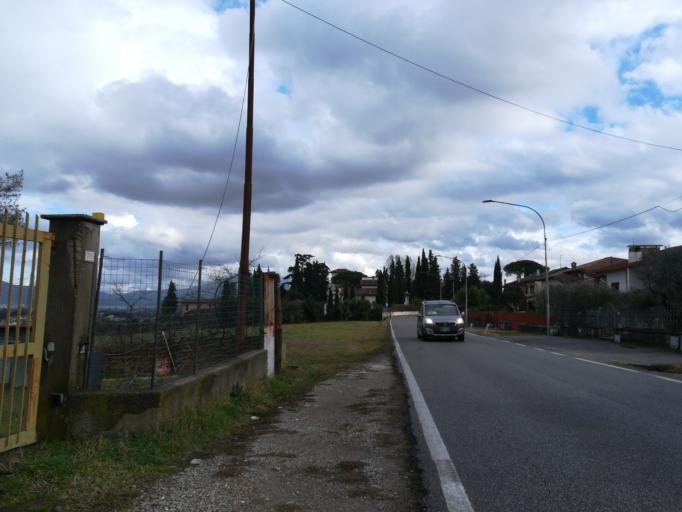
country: IT
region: Tuscany
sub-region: Provincia di Prato
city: Poggio A Caiano
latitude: 43.8085
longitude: 11.0442
